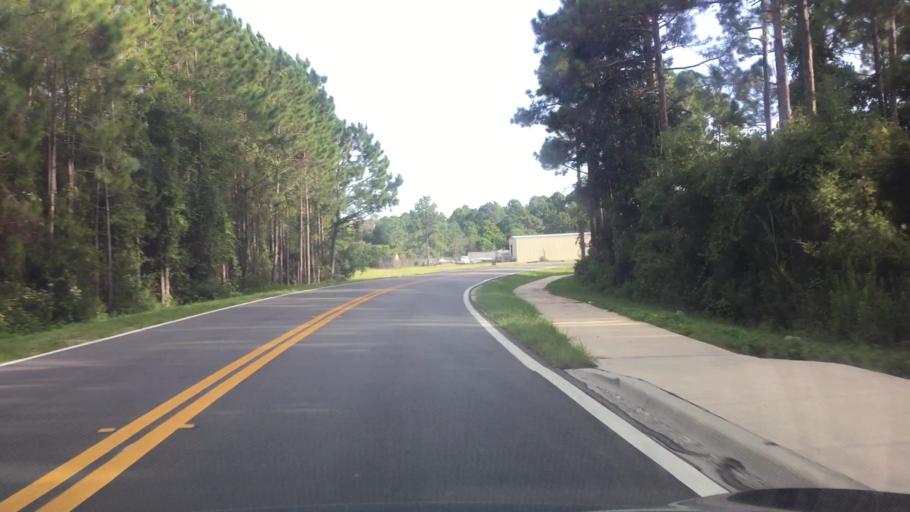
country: US
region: Florida
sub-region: Bay County
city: Panama City Beach
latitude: 30.2001
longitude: -85.8284
